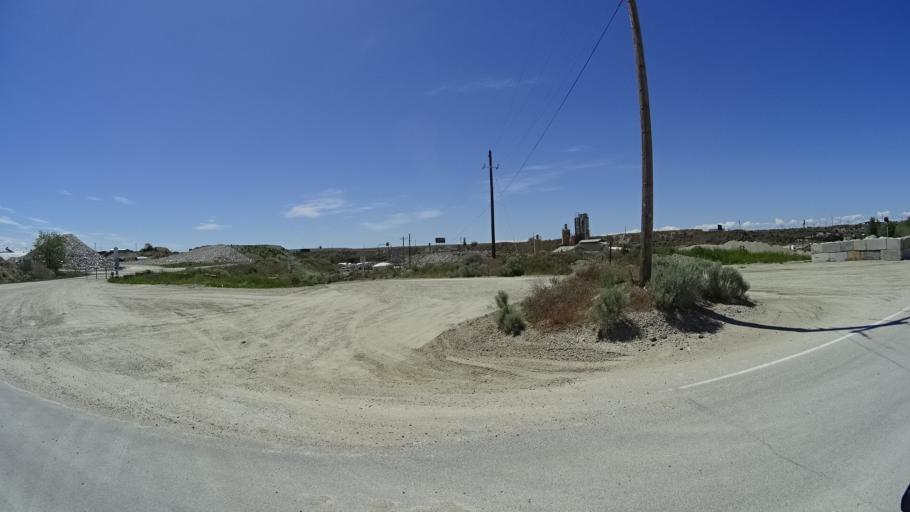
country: US
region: Idaho
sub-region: Ada County
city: Boise
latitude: 43.5604
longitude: -116.1793
